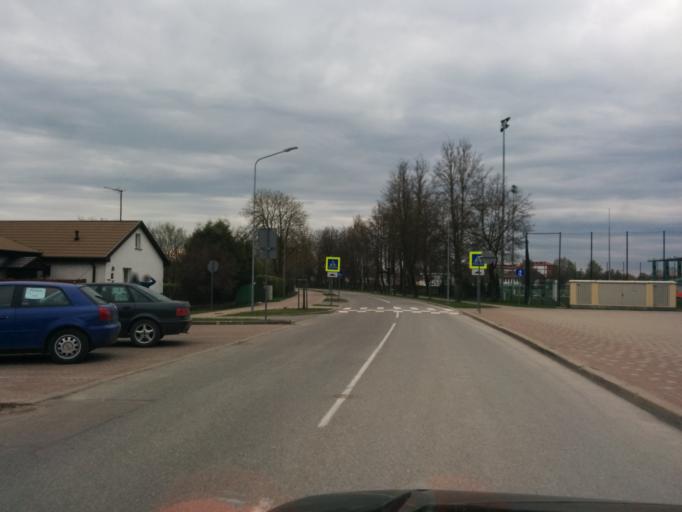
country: LV
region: Ozolnieku
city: Ozolnieki
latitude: 56.6623
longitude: 23.7580
